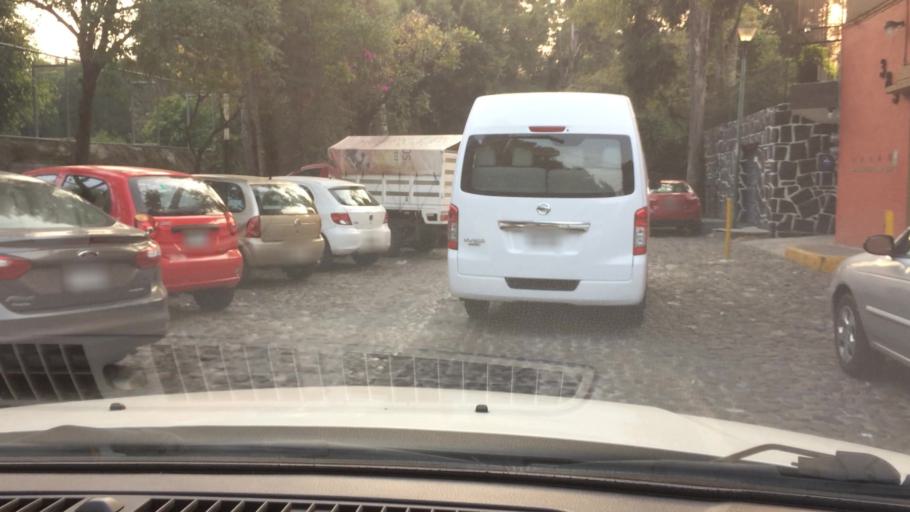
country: MX
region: Mexico City
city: Alvaro Obregon
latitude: 19.3497
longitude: -99.1843
